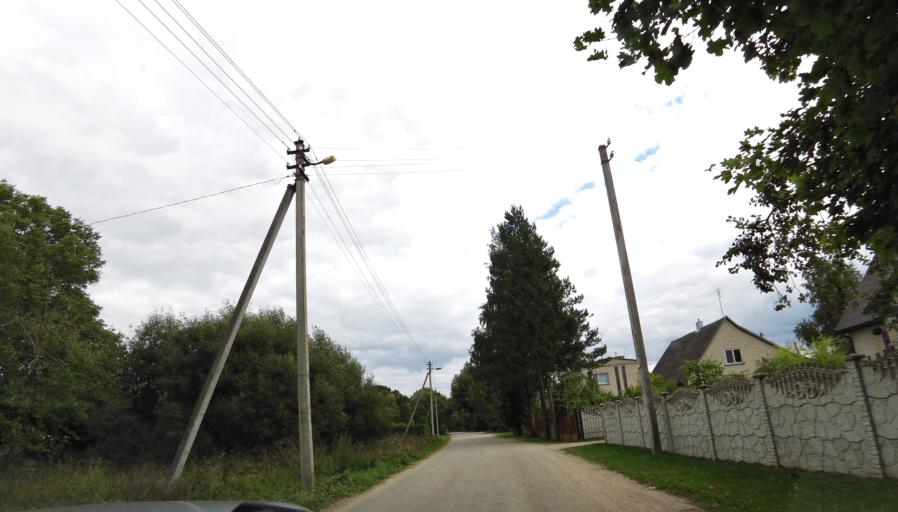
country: LT
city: Linkuva
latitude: 56.0594
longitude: 24.1495
